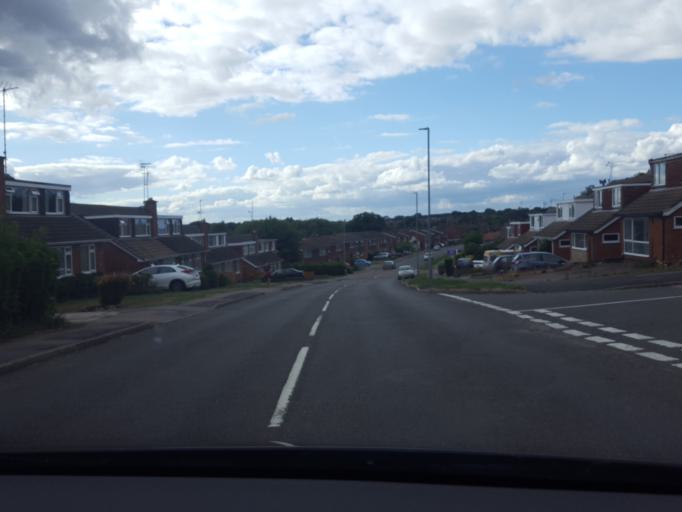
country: GB
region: England
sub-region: Leicestershire
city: Loughborough
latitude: 52.7525
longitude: -1.2211
